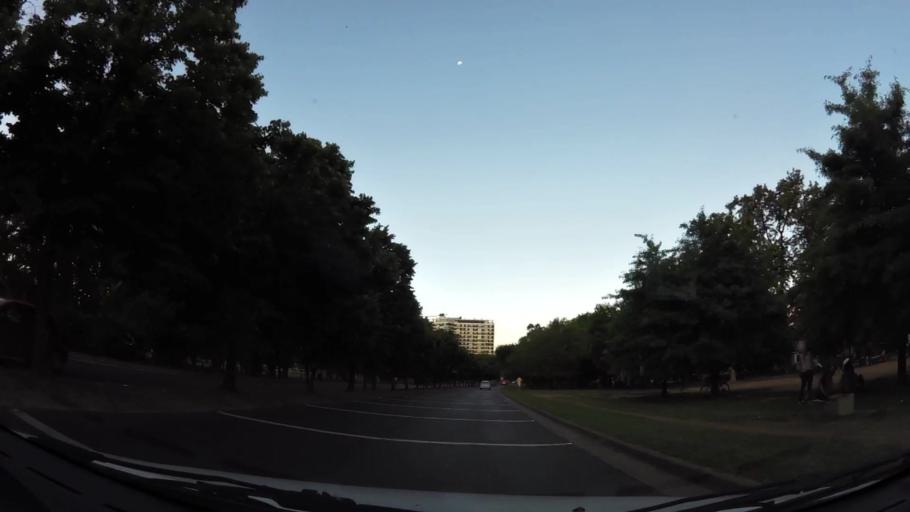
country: AR
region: Buenos Aires
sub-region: Partido de San Isidro
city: San Isidro
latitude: -34.4813
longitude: -58.5098
